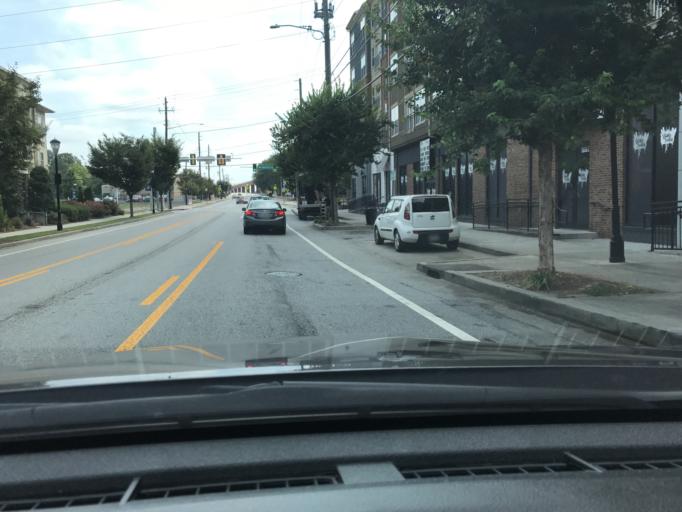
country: US
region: Georgia
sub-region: Fulton County
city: Atlanta
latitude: 33.7500
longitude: -84.3776
